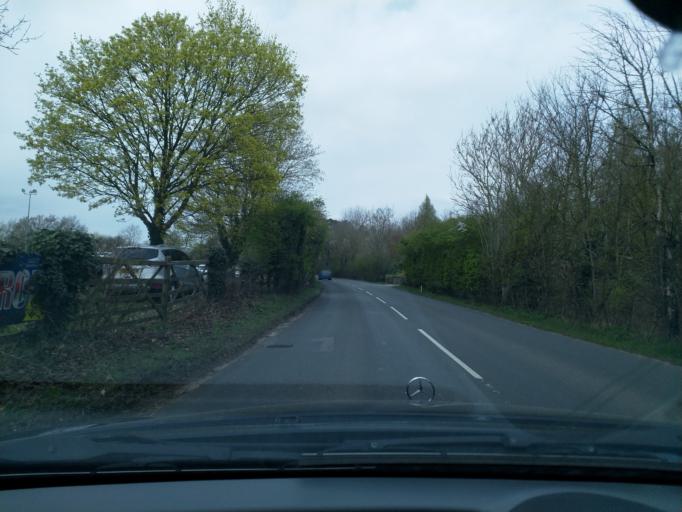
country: GB
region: England
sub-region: Warwickshire
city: Royal Leamington Spa
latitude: 52.3213
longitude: -1.5339
